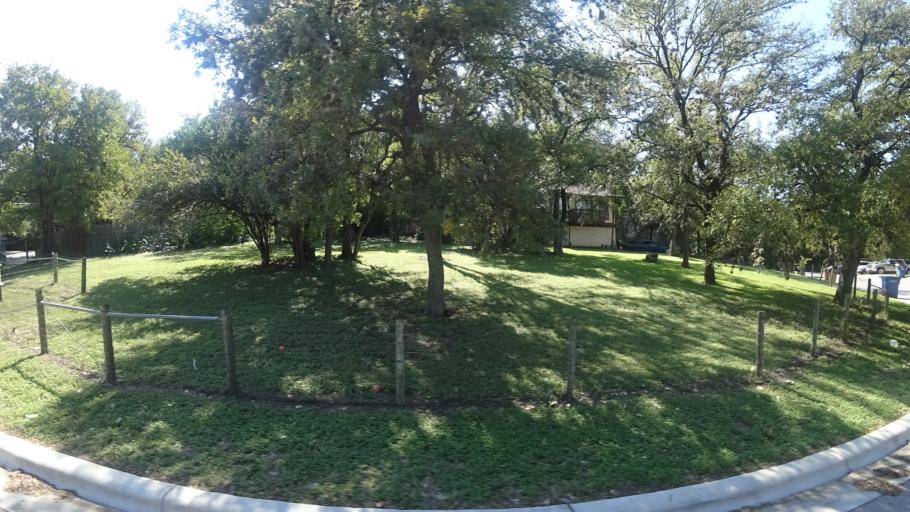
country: US
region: Texas
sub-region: Travis County
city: Austin
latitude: 30.3096
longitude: -97.6776
